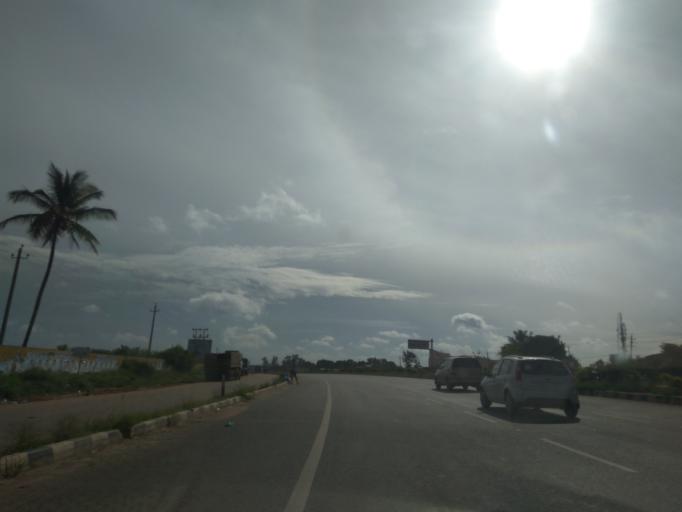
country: IN
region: Karnataka
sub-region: Bangalore Rural
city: Hoskote
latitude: 13.0771
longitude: 77.8074
